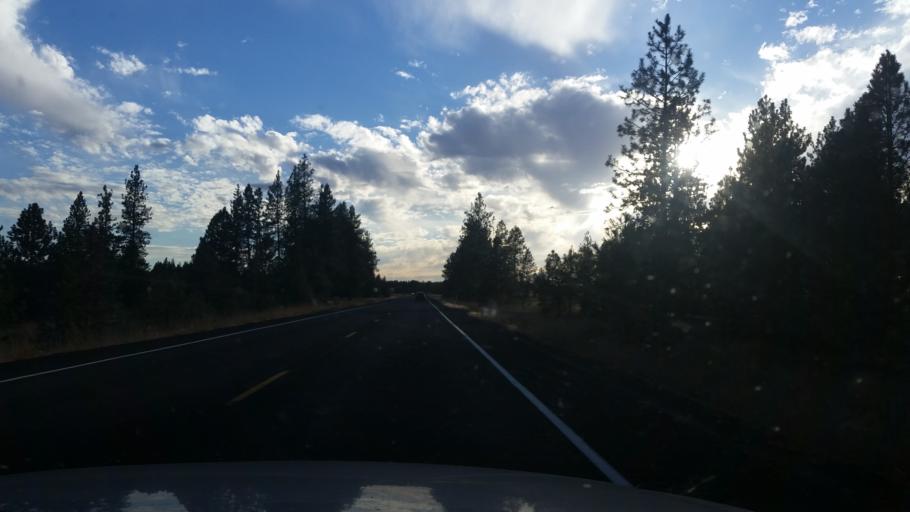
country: US
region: Washington
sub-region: Spokane County
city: Medical Lake
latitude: 47.4429
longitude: -117.7526
